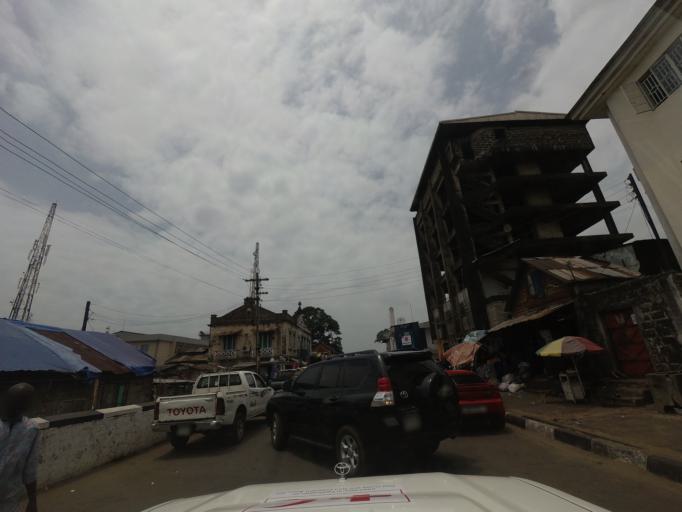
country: SL
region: Western Area
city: Freetown
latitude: 8.4913
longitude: -13.2344
